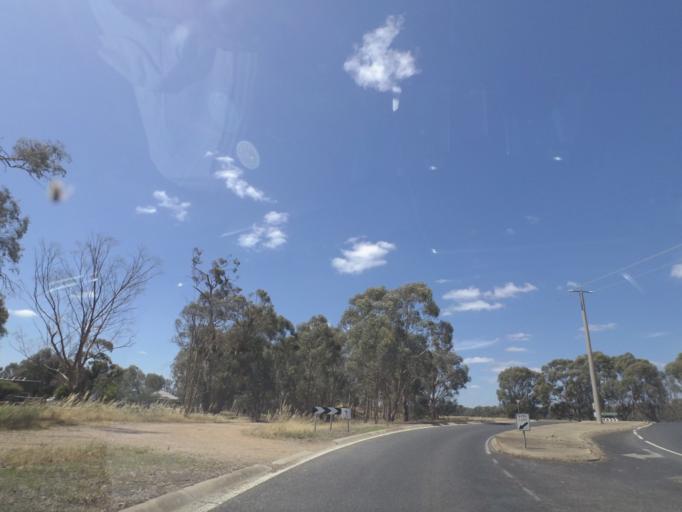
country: AU
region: Victoria
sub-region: Wangaratta
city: Wangaratta
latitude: -36.4070
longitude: 146.2720
